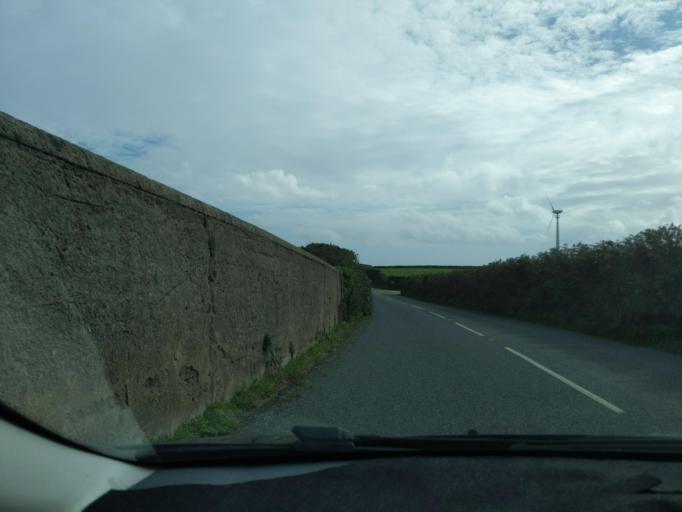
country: GB
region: England
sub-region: Cornwall
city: Mevagissey
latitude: 50.2647
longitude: -4.8293
